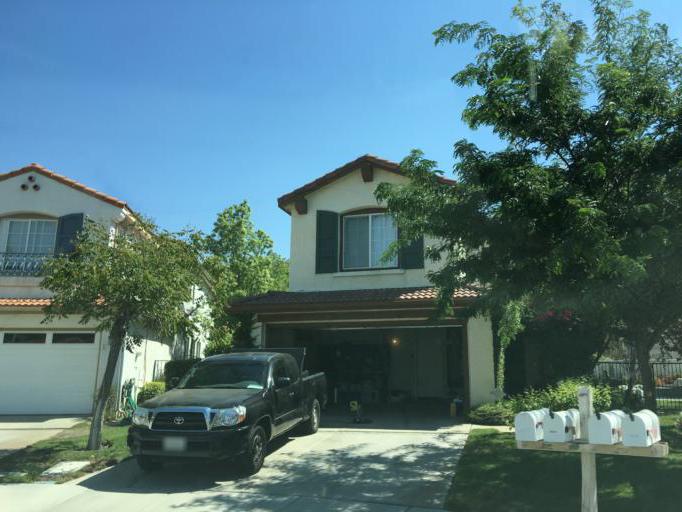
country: US
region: California
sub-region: Los Angeles County
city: Santa Clarita
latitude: 34.3932
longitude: -118.5861
